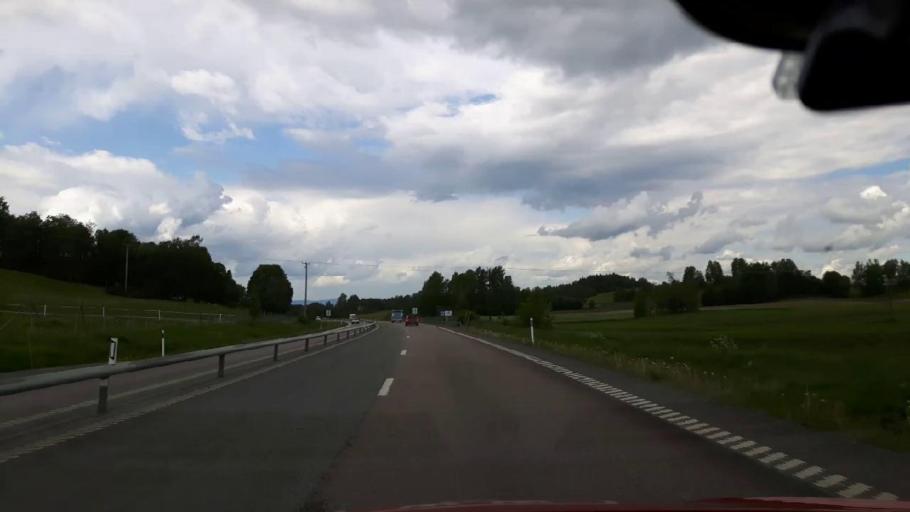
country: SE
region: Jaemtland
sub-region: Krokoms Kommun
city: Krokom
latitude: 63.3070
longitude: 14.4878
